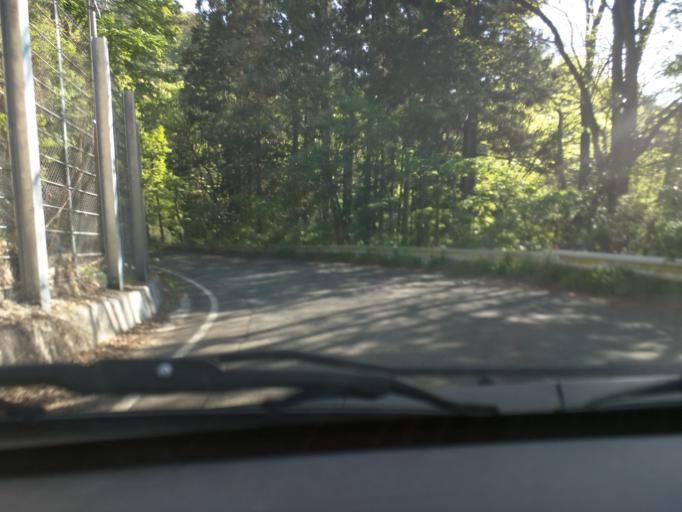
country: JP
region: Nagano
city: Nagano-shi
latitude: 36.6674
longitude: 138.1808
